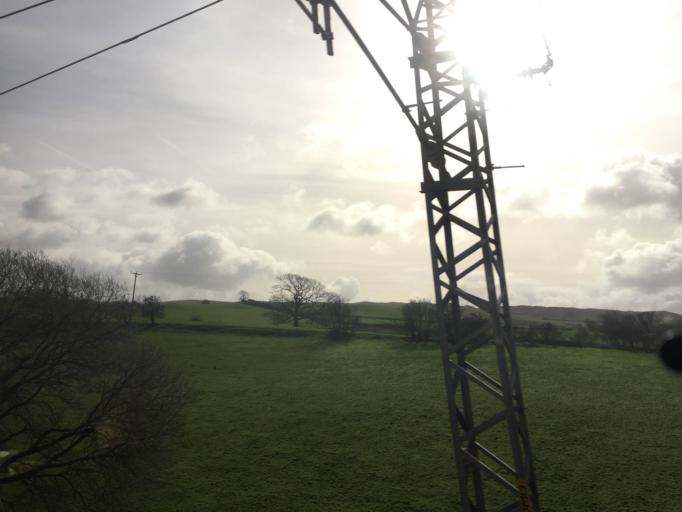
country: GB
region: England
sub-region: Cumbria
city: Kendal
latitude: 54.3563
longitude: -2.6628
